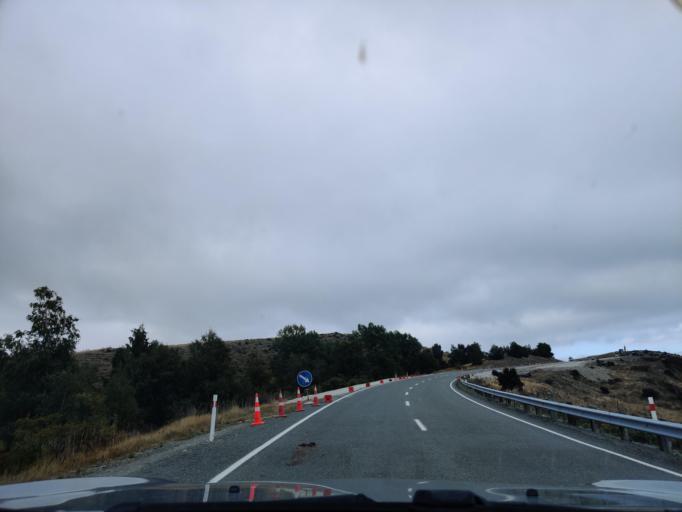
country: NZ
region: Canterbury
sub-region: Timaru District
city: Pleasant Point
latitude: -44.1772
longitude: 170.2036
